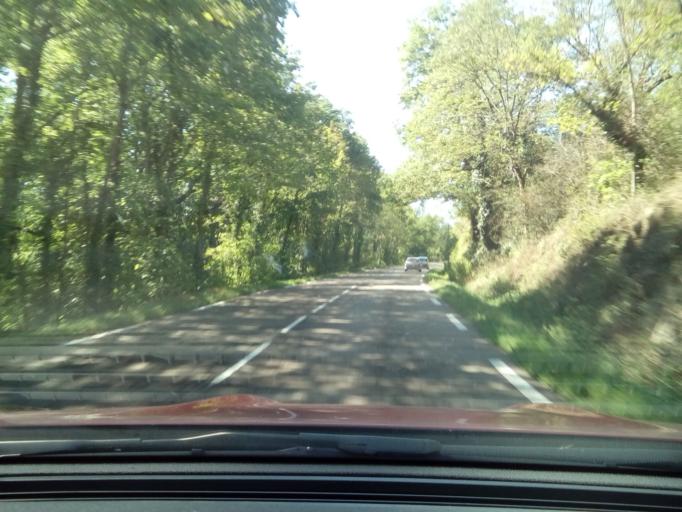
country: FR
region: Rhone-Alpes
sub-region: Departement du Rhone
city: Saint-Verand
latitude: 45.9043
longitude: 4.5292
